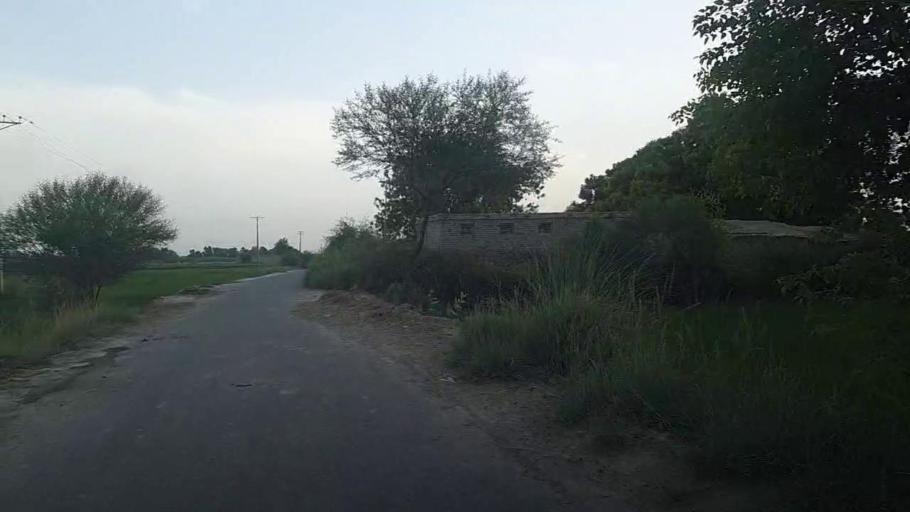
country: PK
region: Sindh
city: Ubauro
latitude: 28.3554
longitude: 69.7818
